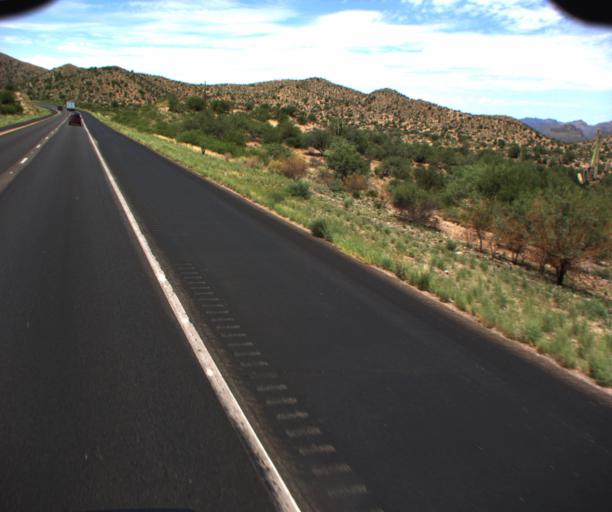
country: US
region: Arizona
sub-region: Pinal County
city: Superior
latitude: 33.2738
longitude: -111.1959
